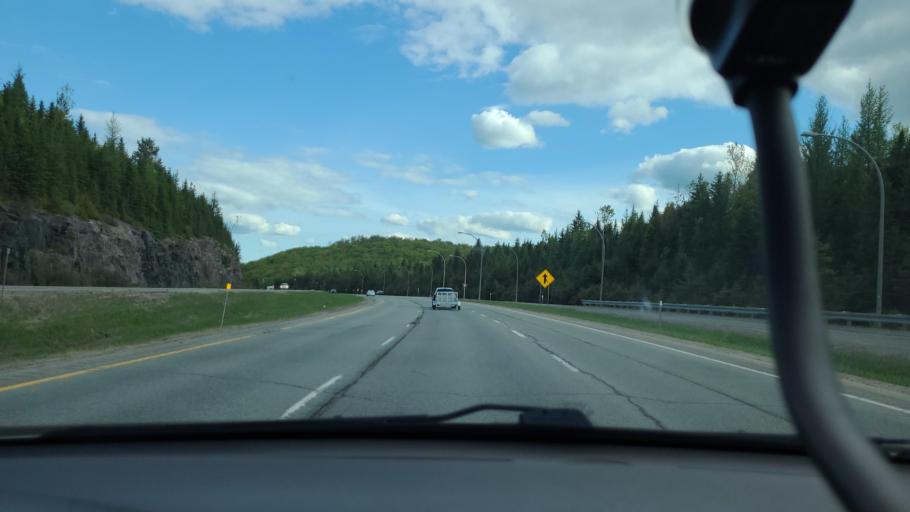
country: CA
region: Quebec
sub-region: Laurentides
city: Sainte-Agathe-des-Monts
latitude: 46.0370
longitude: -74.2698
